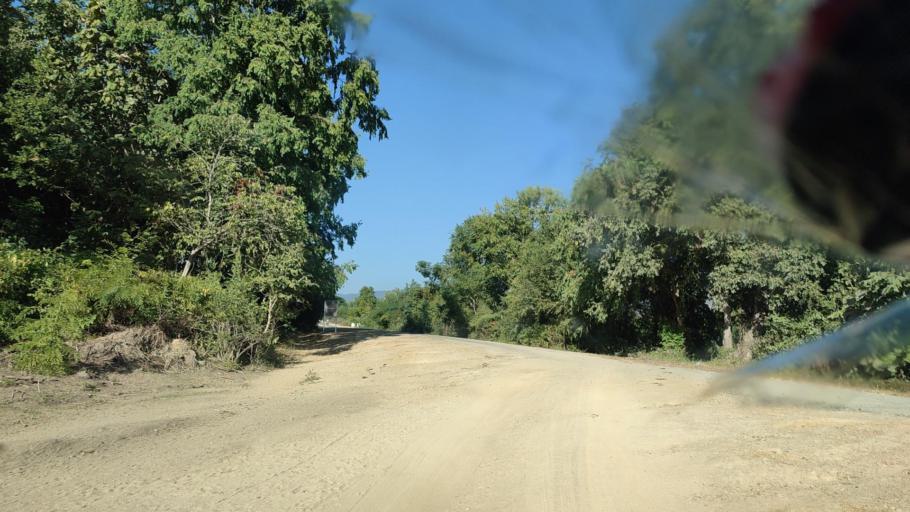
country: MM
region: Mandalay
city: Yamethin
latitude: 20.3093
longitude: 96.2576
